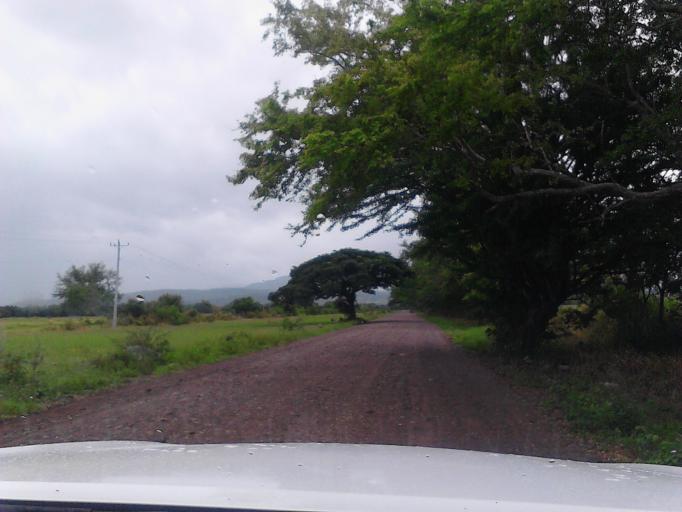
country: NI
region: Matagalpa
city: Ciudad Dario
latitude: 12.8956
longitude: -86.1505
